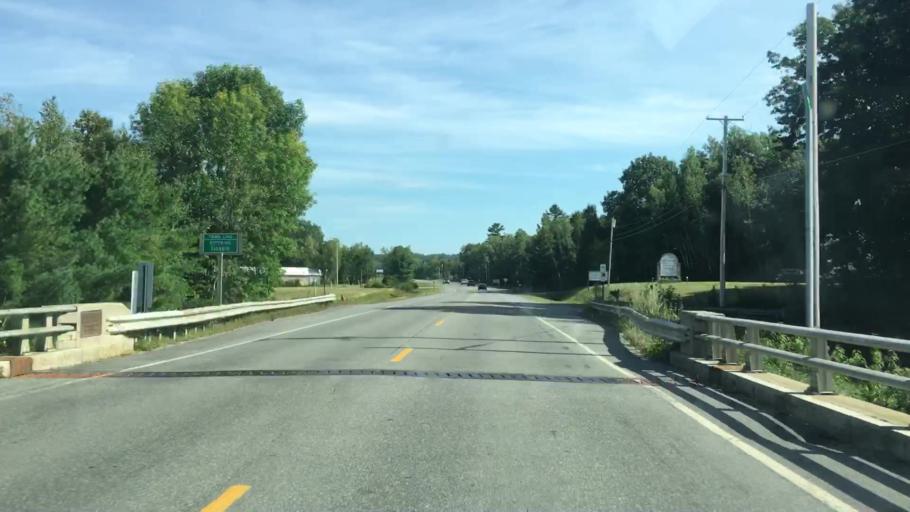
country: US
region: Maine
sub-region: Penobscot County
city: Lincoln
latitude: 45.3614
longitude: -68.5465
